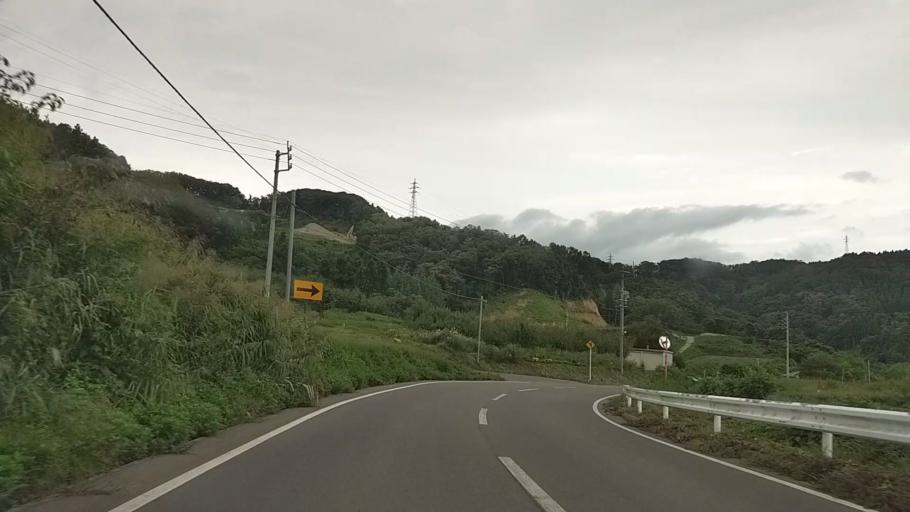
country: JP
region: Nagano
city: Nakano
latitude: 36.7835
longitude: 138.3331
